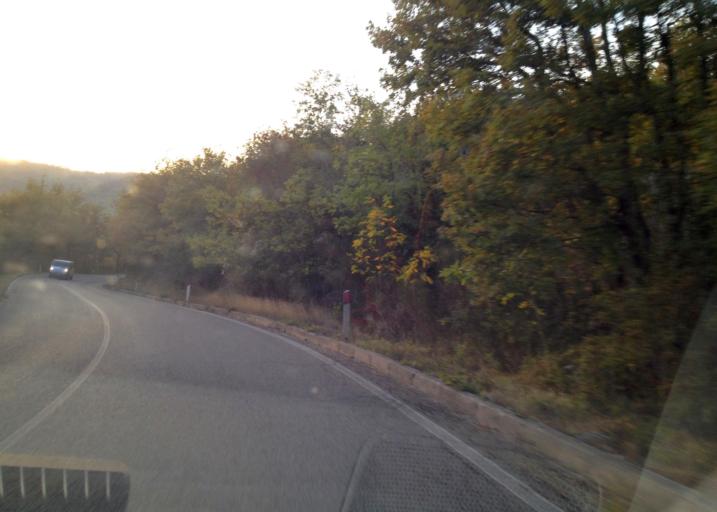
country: IT
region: Tuscany
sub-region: Provincia di Siena
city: Castellina in Chianti
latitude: 43.5034
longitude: 11.2968
